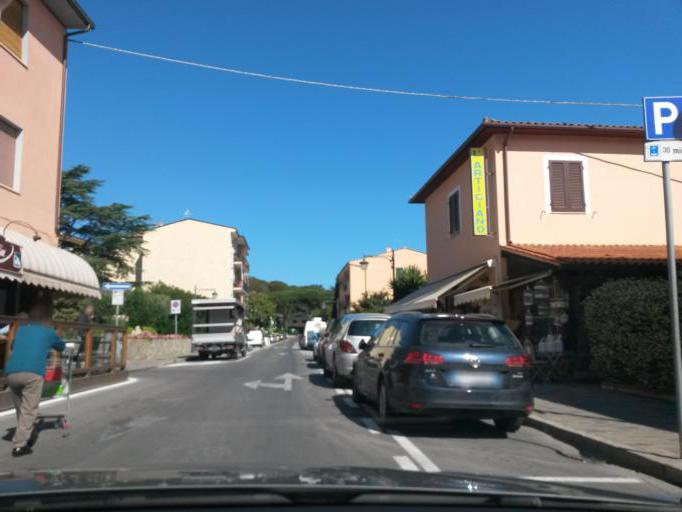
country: IT
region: Tuscany
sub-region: Provincia di Livorno
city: Marciana Marina
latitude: 42.8048
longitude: 10.1975
